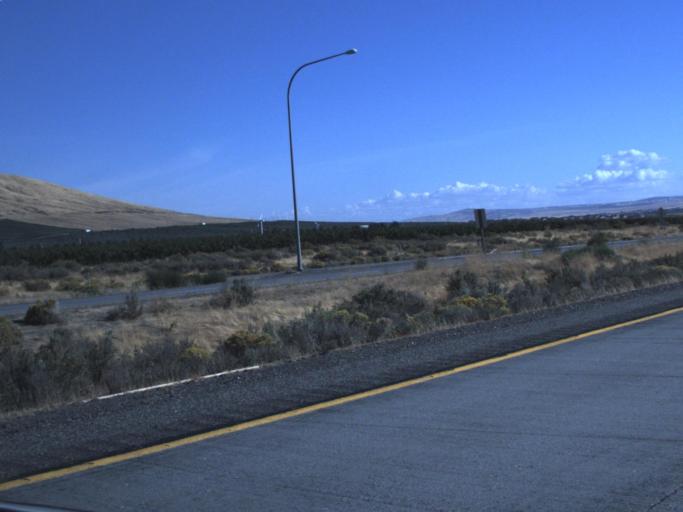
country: US
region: Washington
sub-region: Benton County
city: West Richland
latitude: 46.2418
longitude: -119.3611
